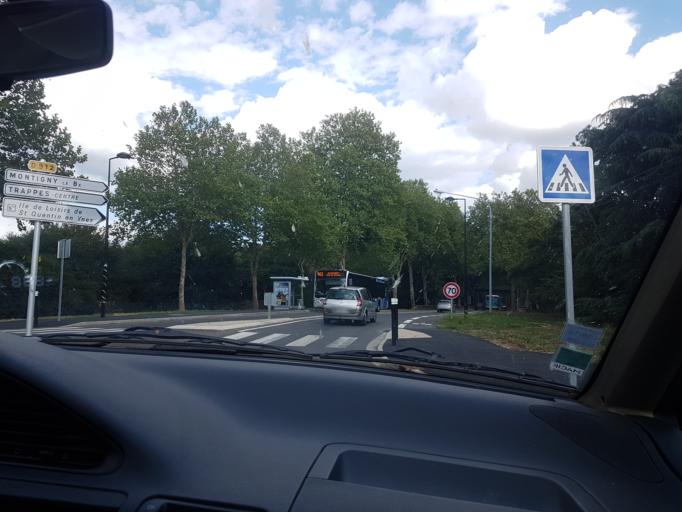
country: FR
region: Ile-de-France
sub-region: Departement des Yvelines
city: Elancourt
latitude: 48.7853
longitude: 1.9868
